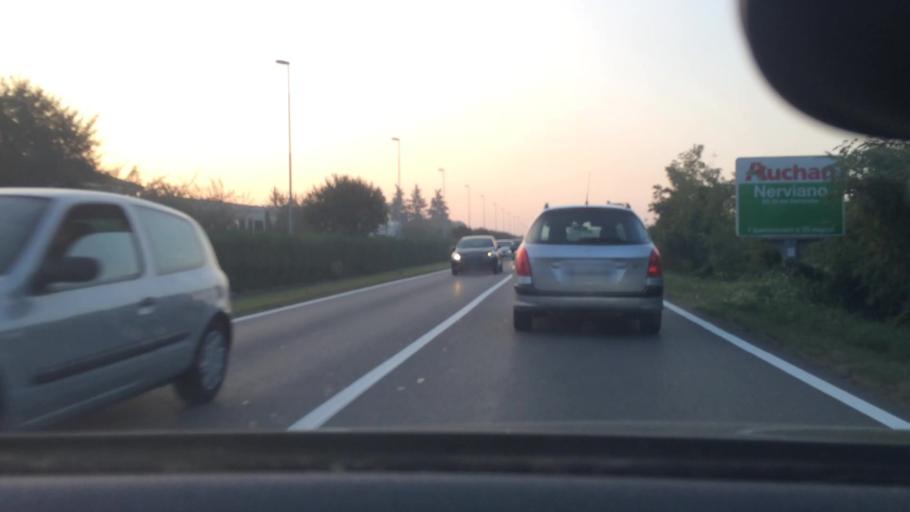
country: IT
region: Lombardy
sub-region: Citta metropolitana di Milano
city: Parabiago
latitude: 45.5465
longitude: 8.9530
